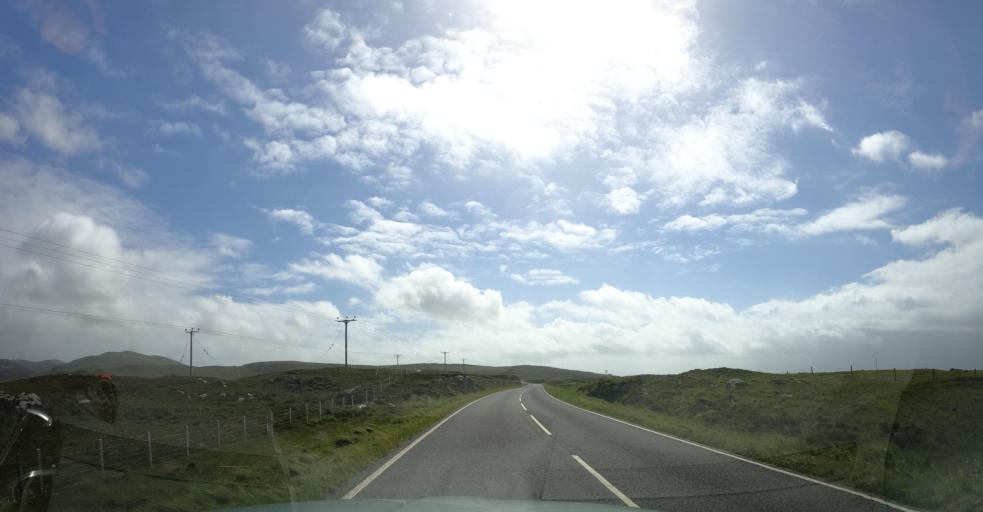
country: GB
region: Scotland
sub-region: Eilean Siar
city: Isle of South Uist
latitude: 57.2448
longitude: -7.3826
